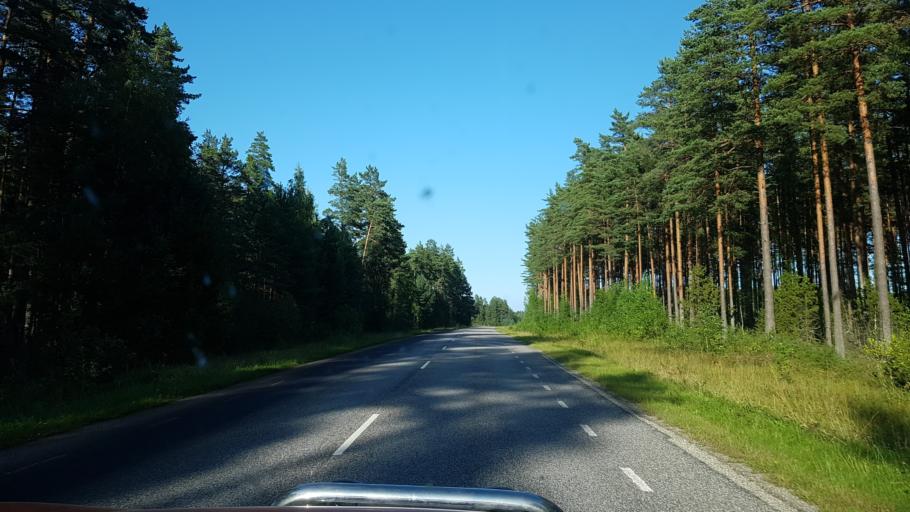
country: RU
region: Pskov
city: Pechory
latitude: 57.8197
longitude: 27.3453
